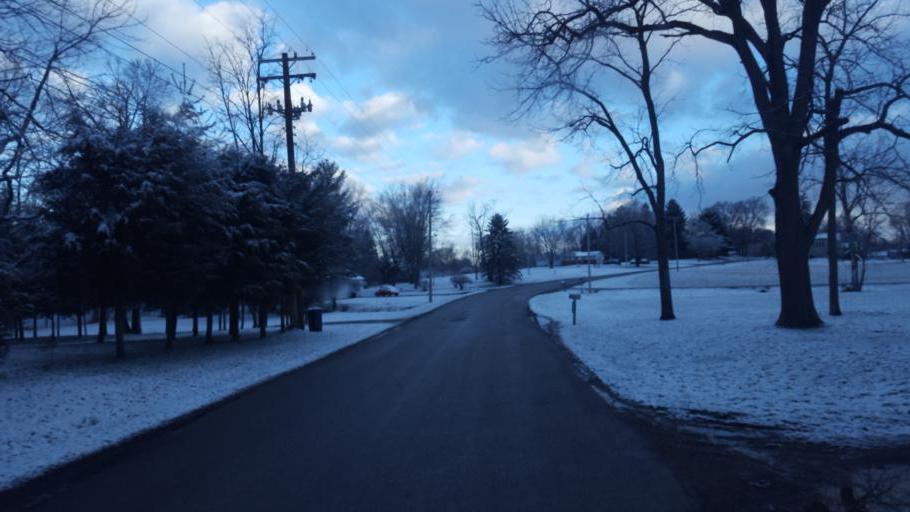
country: US
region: Ohio
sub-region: Morrow County
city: Mount Gilead
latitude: 40.5648
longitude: -82.8431
